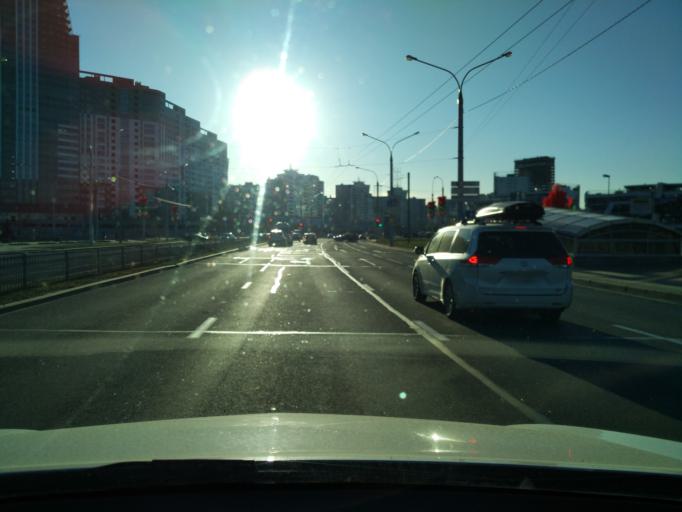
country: BY
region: Minsk
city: Zhdanovichy
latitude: 53.9375
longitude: 27.4814
